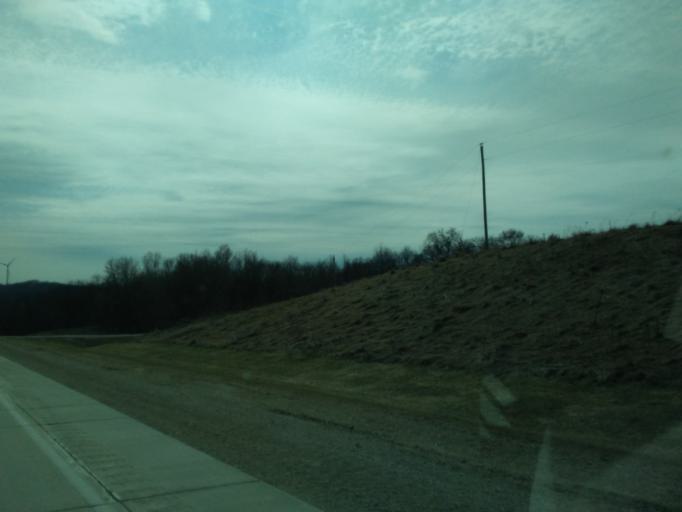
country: US
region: Iowa
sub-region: Winneshiek County
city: Decorah
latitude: 43.3305
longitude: -91.8128
